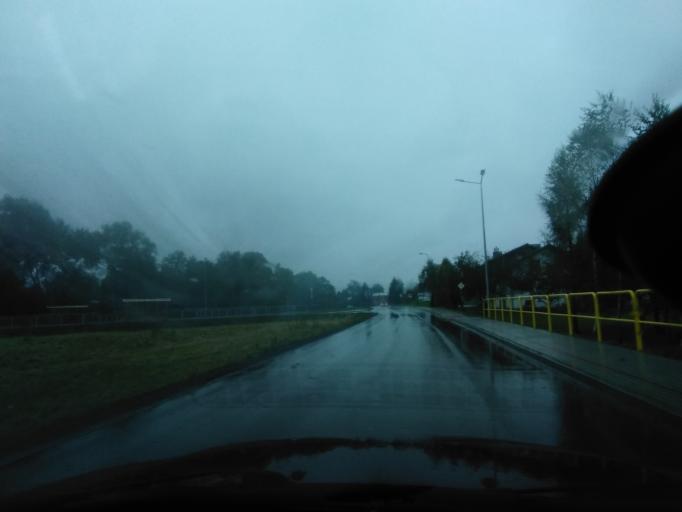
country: PL
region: Subcarpathian Voivodeship
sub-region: Powiat krosnienski
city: Korczyna
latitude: 49.6989
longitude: 21.8109
